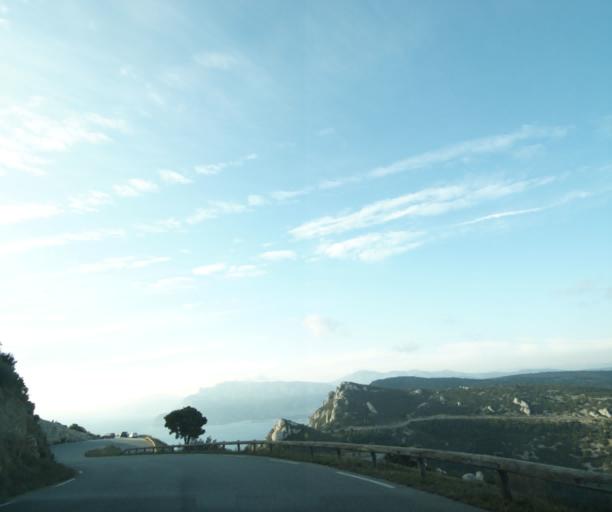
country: FR
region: Provence-Alpes-Cote d'Azur
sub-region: Departement des Bouches-du-Rhone
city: Cassis
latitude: 43.1841
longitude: 5.5653
